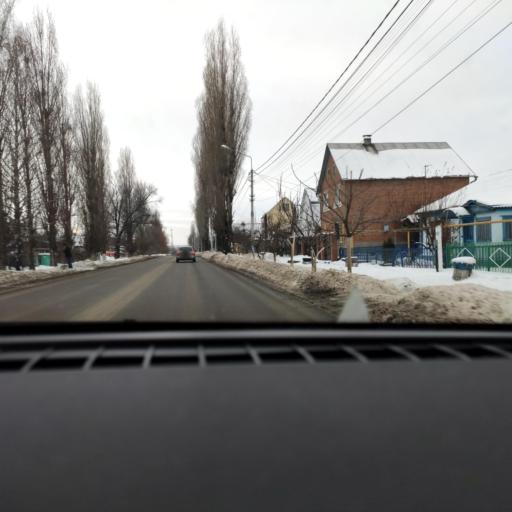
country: RU
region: Voronezj
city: Maslovka
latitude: 51.5449
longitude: 39.2327
